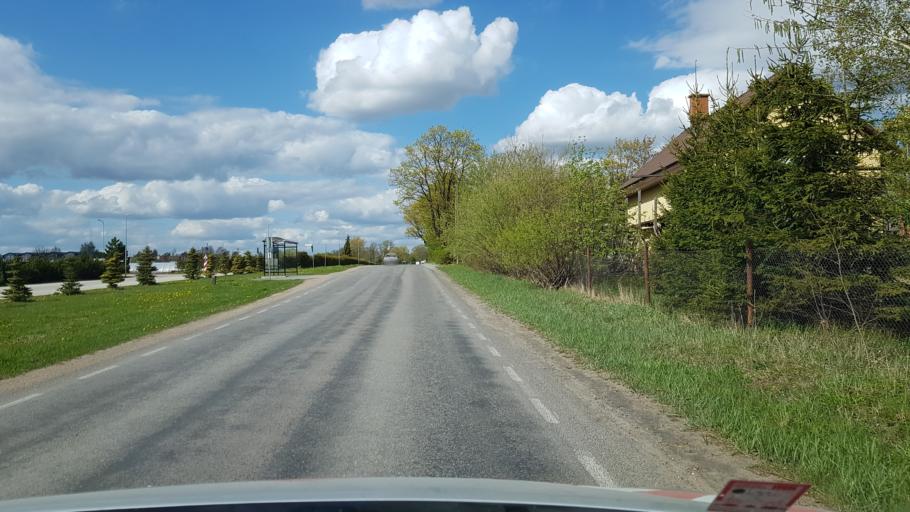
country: EE
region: Tartu
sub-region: Tartu linn
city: Tartu
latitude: 58.3653
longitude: 26.7988
